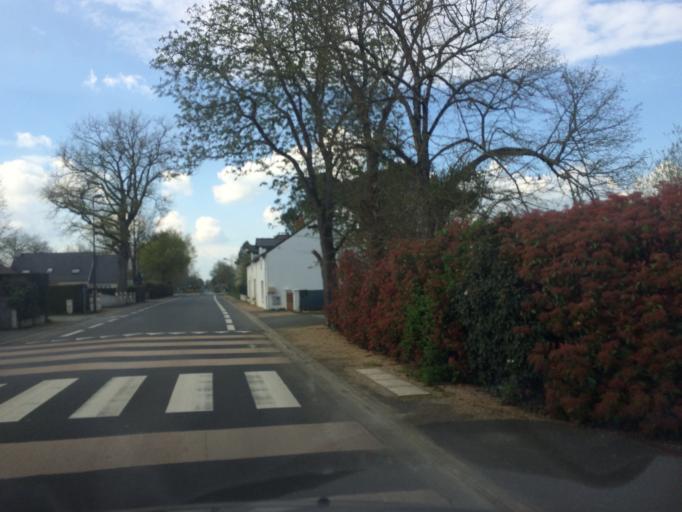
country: FR
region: Pays de la Loire
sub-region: Departement de la Loire-Atlantique
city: Heric
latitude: 47.4190
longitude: -1.6558
